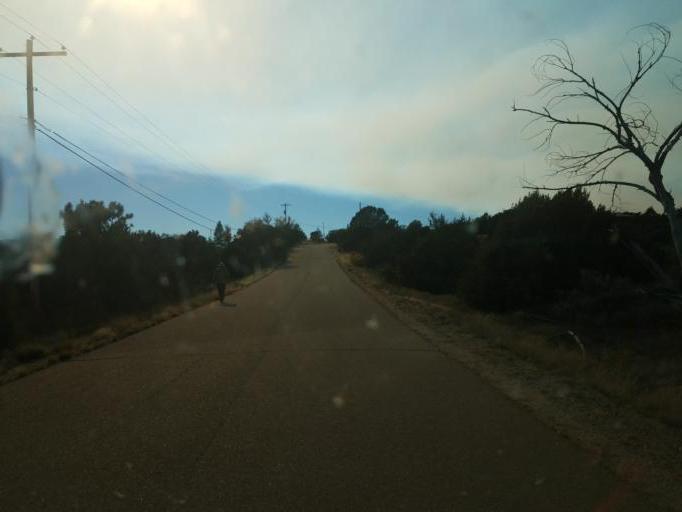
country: US
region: New Mexico
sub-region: Los Alamos County
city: White Rock
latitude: 35.8044
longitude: -106.2152
